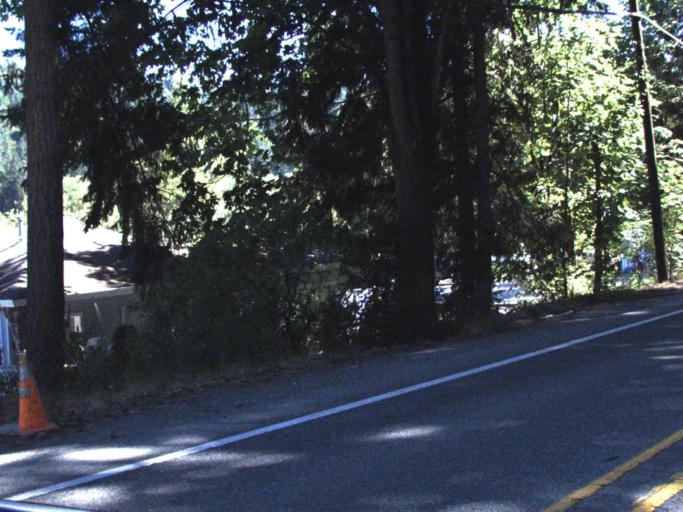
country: US
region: Washington
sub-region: King County
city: East Renton Highlands
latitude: 47.4975
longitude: -122.1072
